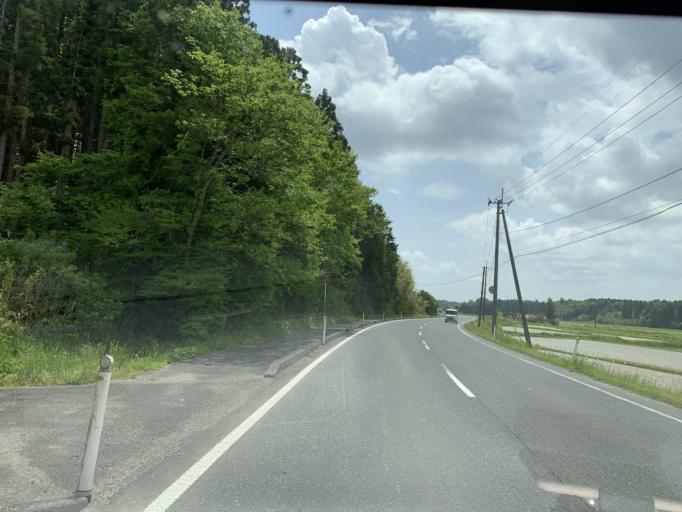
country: JP
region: Miyagi
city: Furukawa
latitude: 38.6842
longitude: 140.9743
